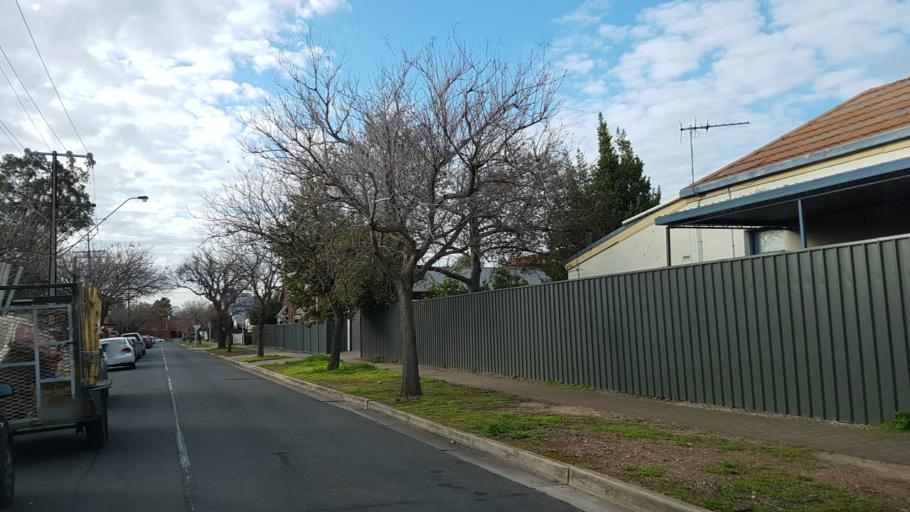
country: AU
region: South Australia
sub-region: Prospect
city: Prospect
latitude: -34.8888
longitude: 138.5976
